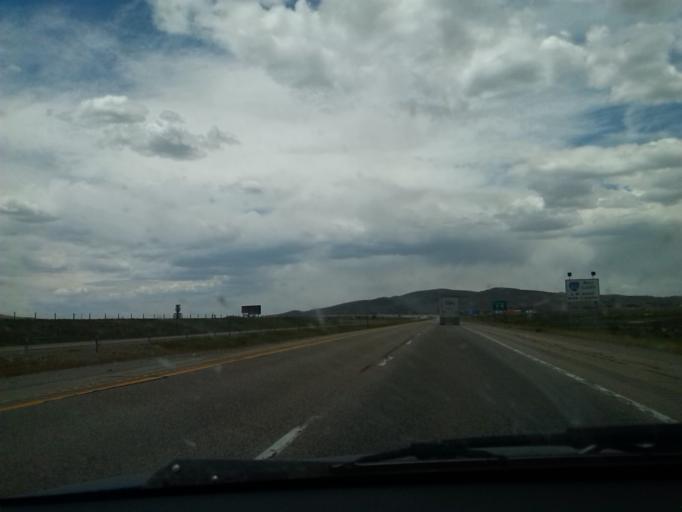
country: US
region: Wyoming
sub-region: Carbon County
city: Rawlins
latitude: 41.7874
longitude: -107.1866
